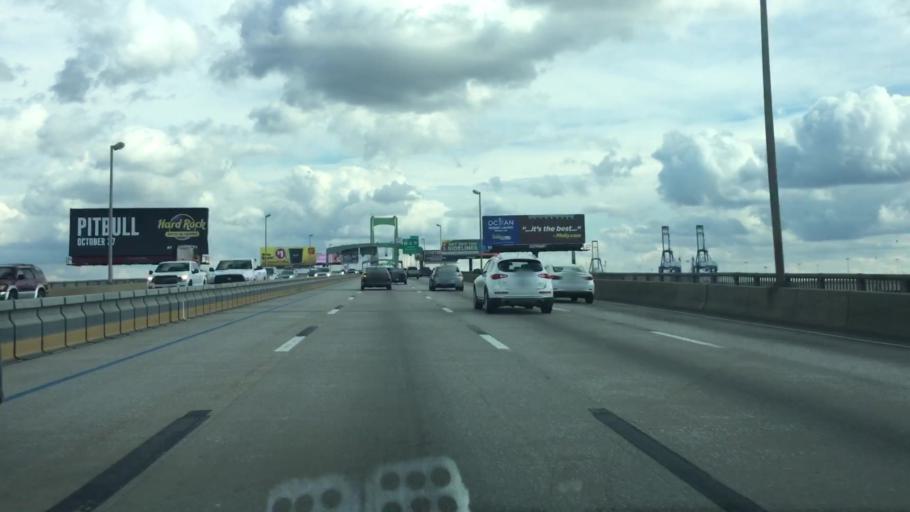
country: US
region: New Jersey
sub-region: Camden County
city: Camden
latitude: 39.9080
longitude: -75.1460
